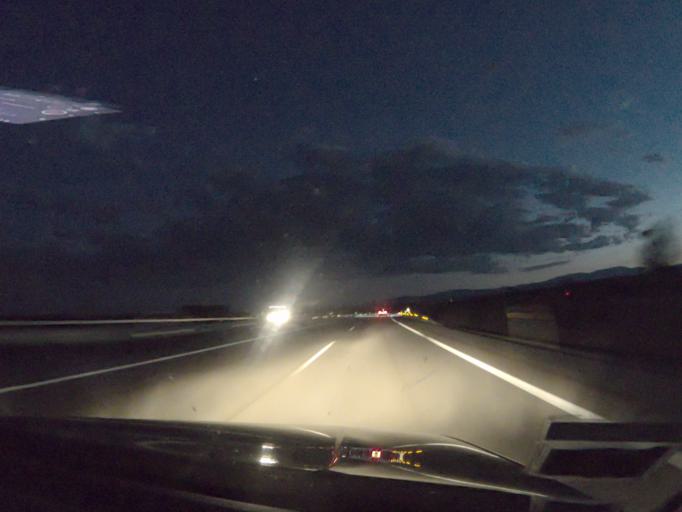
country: ES
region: Castille and Leon
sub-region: Provincia de Leon
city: Brazuelo
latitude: 42.5055
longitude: -6.1181
